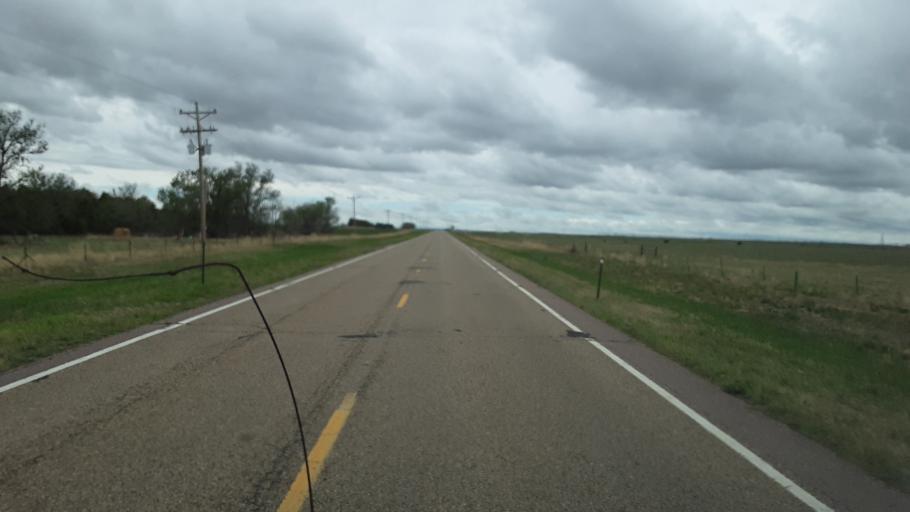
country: US
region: Colorado
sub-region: El Paso County
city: Ellicott
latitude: 38.8397
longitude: -103.9694
